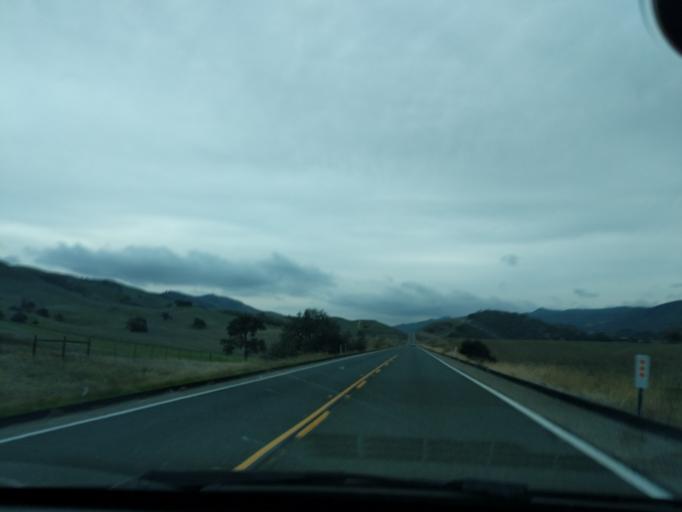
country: US
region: California
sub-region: San Benito County
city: Ridgemark
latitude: 36.6617
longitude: -121.2457
